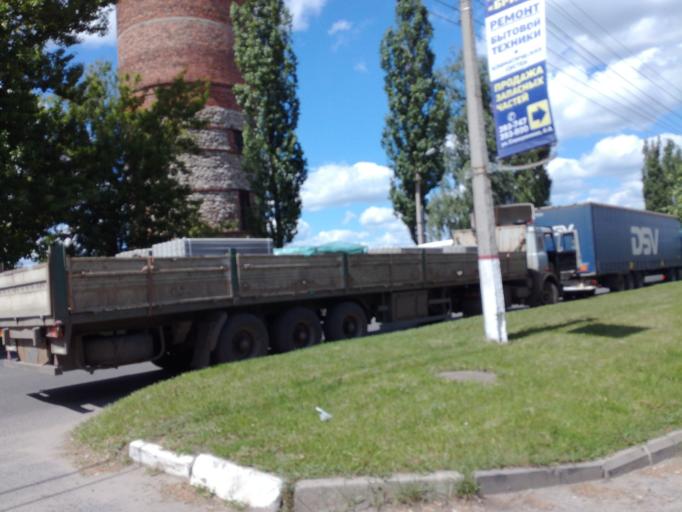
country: RU
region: Kursk
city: Kursk
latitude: 51.7518
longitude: 36.2360
